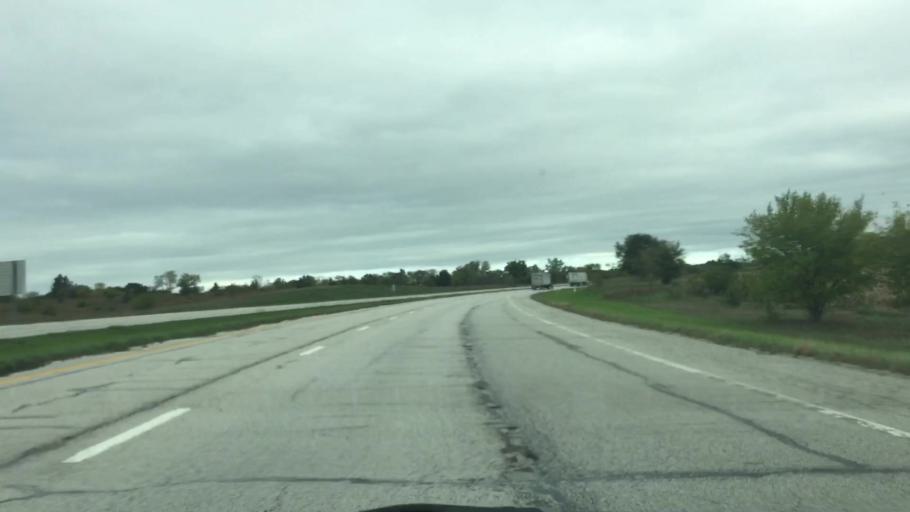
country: US
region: Missouri
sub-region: Harrison County
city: Bethany
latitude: 40.0800
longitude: -94.0930
